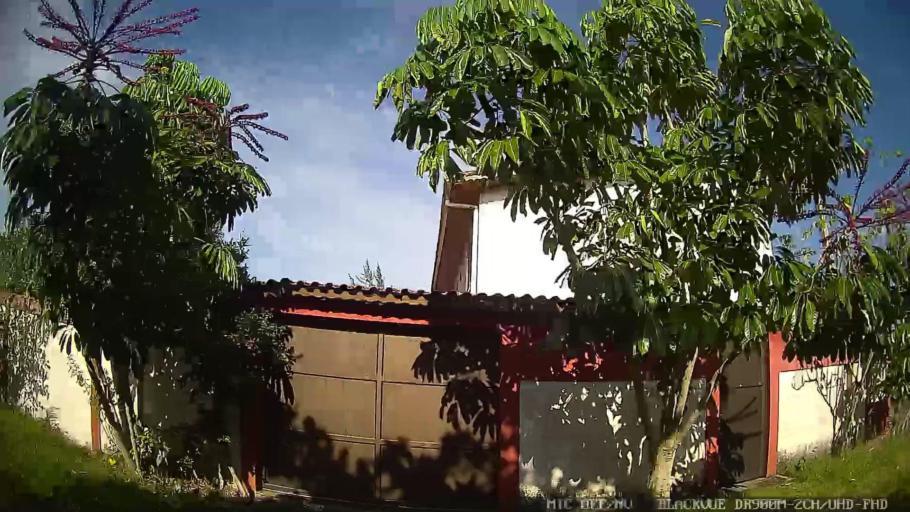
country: BR
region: Sao Paulo
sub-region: Iguape
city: Iguape
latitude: -24.7605
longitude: -47.5760
